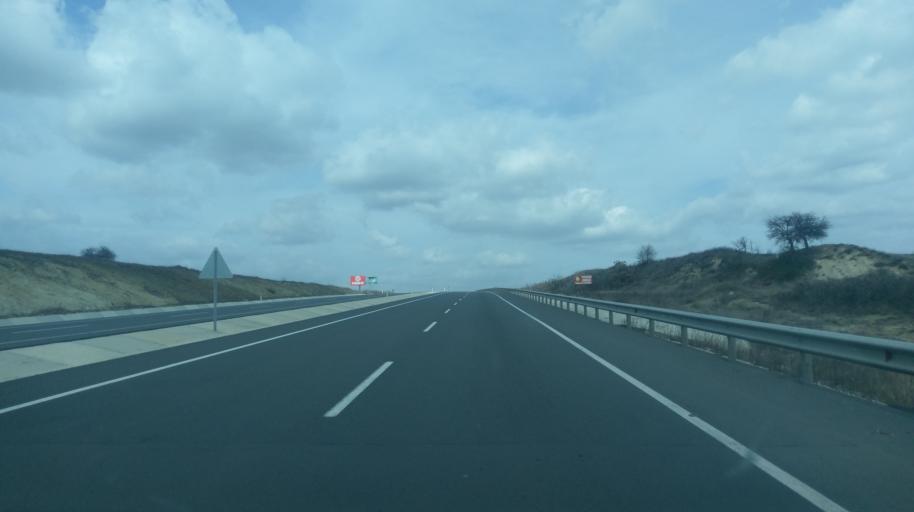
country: TR
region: Edirne
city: Kesan
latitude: 40.9359
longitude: 26.6364
